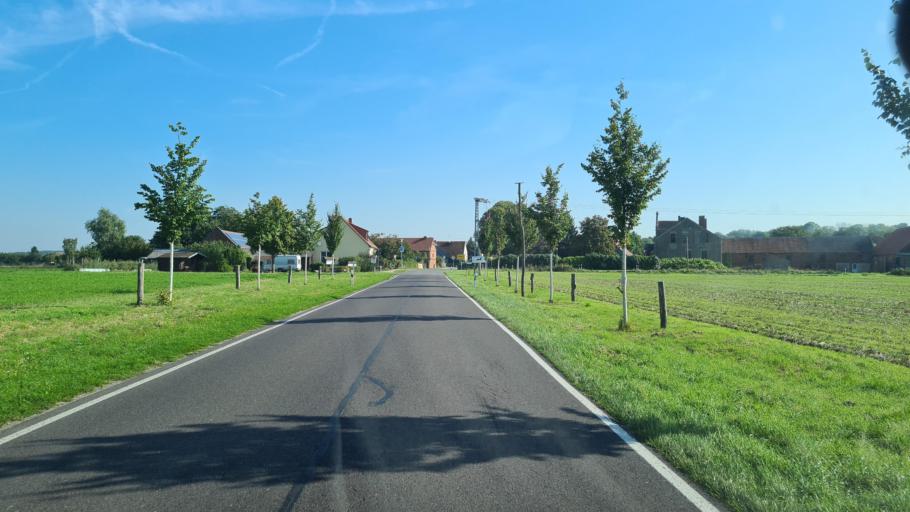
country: DE
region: Brandenburg
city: Pessin
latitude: 52.6703
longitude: 12.6363
